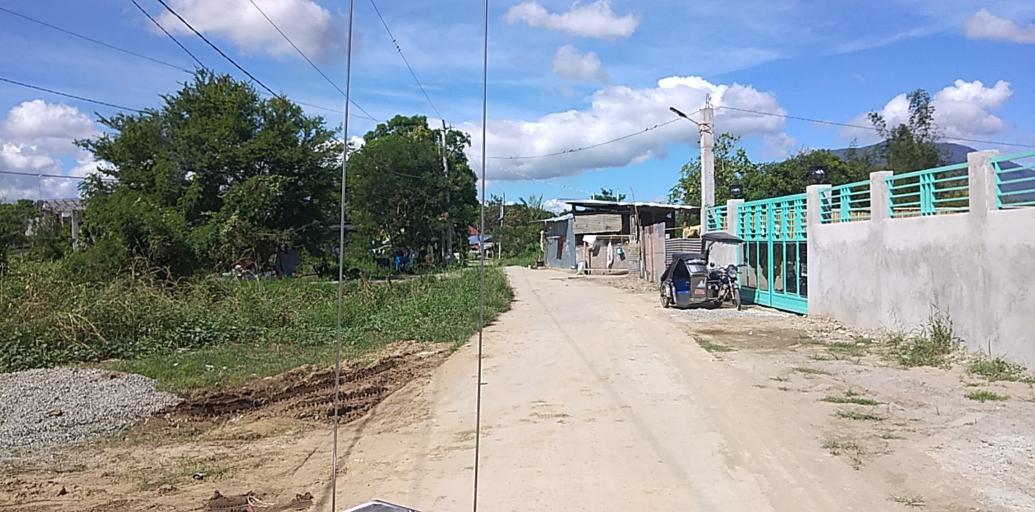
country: PH
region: Central Luzon
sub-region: Province of Pampanga
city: Arayat
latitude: 15.1273
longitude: 120.7820
